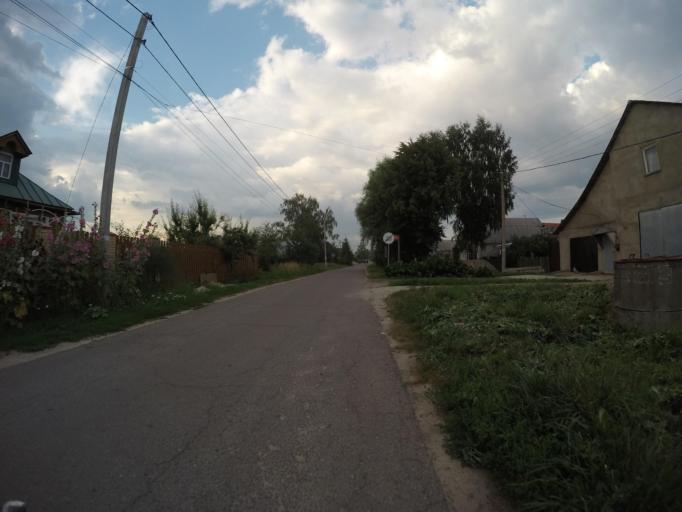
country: RU
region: Moskovskaya
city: Rechitsy
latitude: 55.5968
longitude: 38.5178
